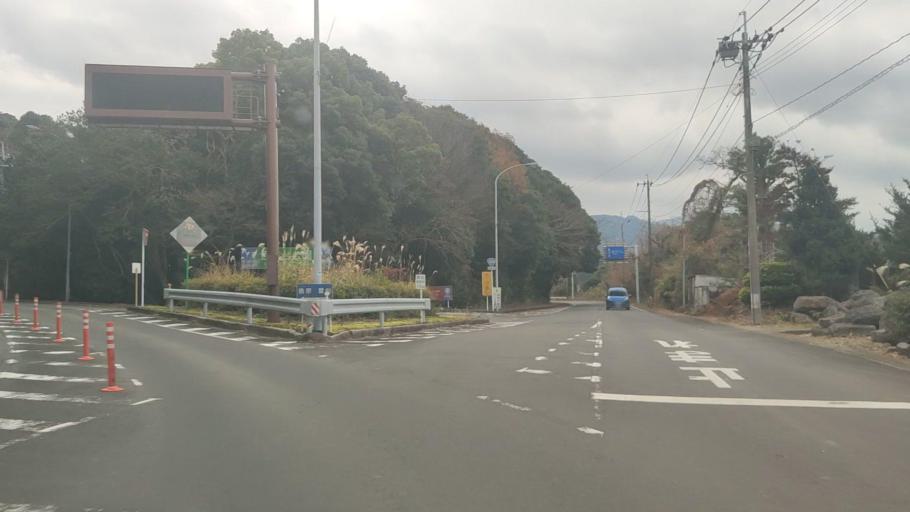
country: JP
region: Nagasaki
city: Shimabara
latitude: 32.8244
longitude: 130.2916
